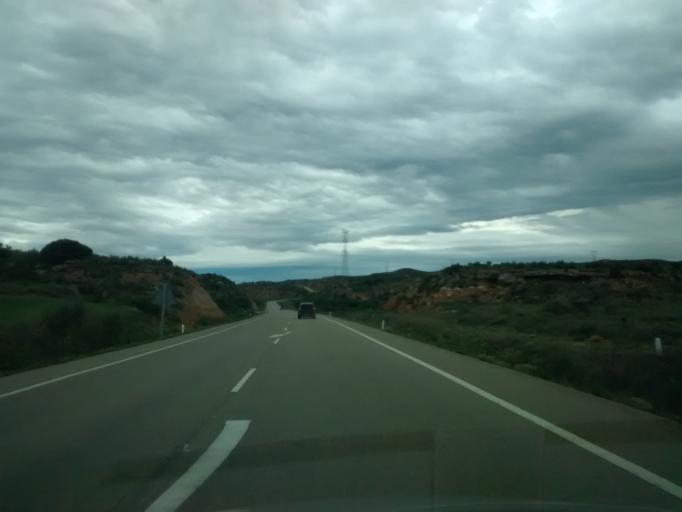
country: ES
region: Aragon
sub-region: Provincia de Zaragoza
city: Caspe
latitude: 41.1915
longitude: 0.0461
